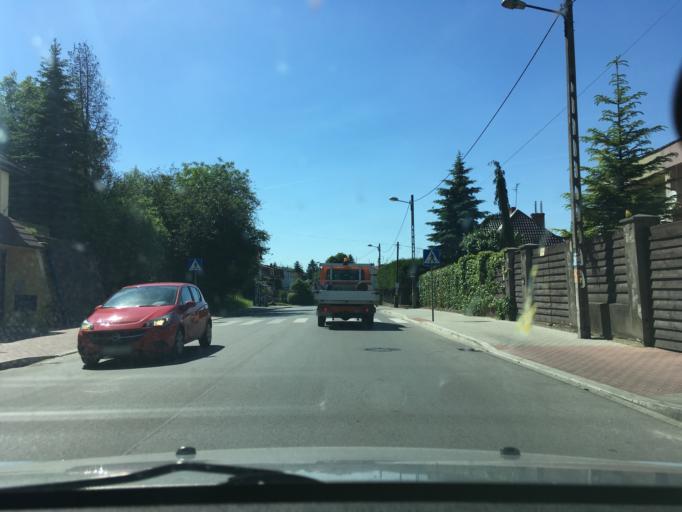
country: PL
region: Lesser Poland Voivodeship
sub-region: Krakow
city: Krakow
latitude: 50.0607
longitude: 19.8924
